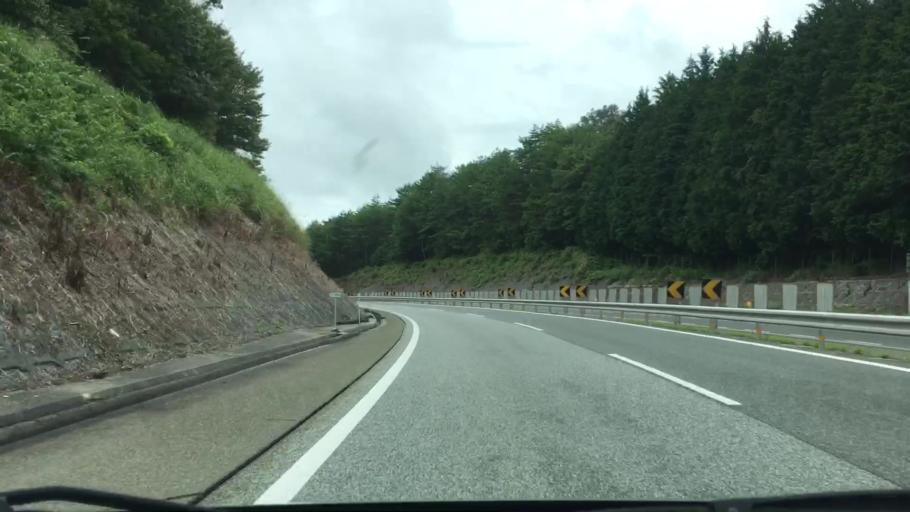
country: JP
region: Hiroshima
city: Shobara
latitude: 34.8731
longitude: 133.1436
